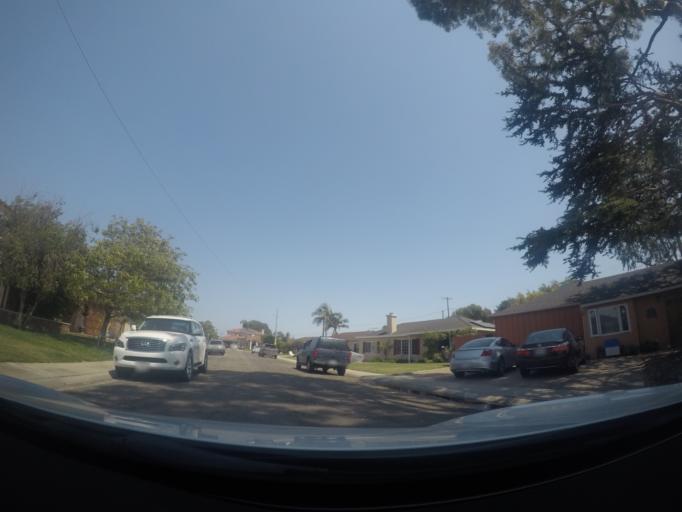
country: US
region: California
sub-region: Los Angeles County
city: Torrance
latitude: 33.8221
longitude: -118.3640
